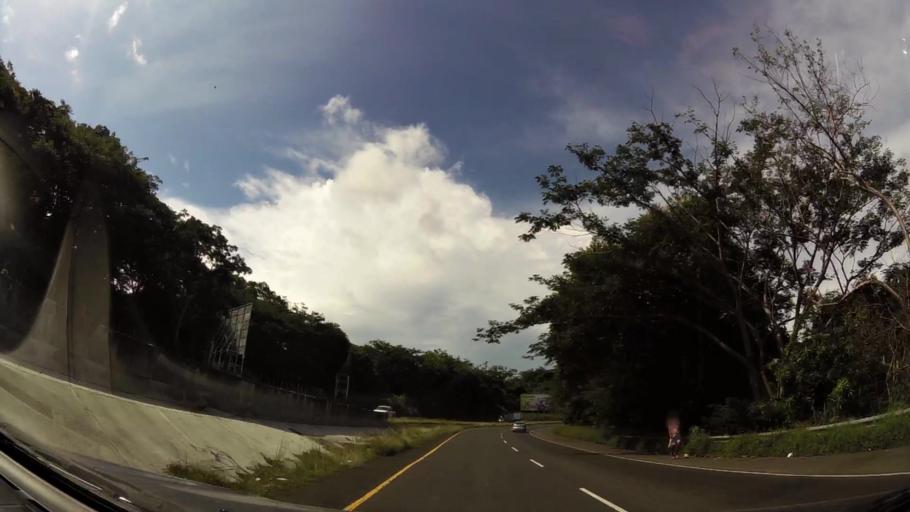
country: PA
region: Panama
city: Capira
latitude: 8.7062
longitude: -79.8703
